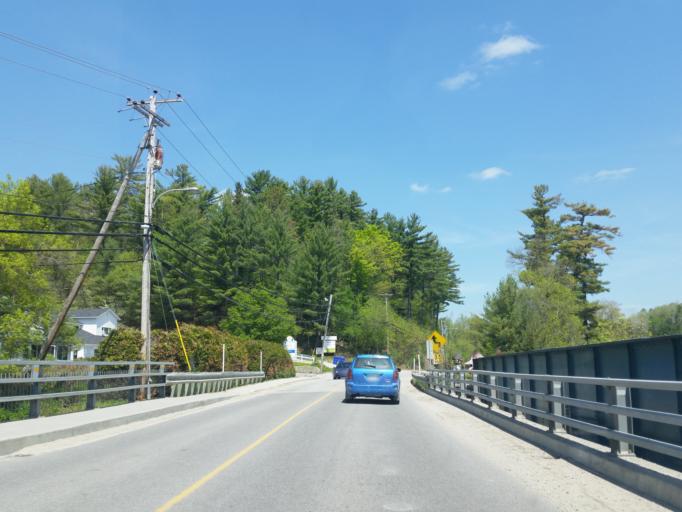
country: CA
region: Quebec
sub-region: Outaouais
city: Wakefield
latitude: 45.6370
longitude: -75.9301
